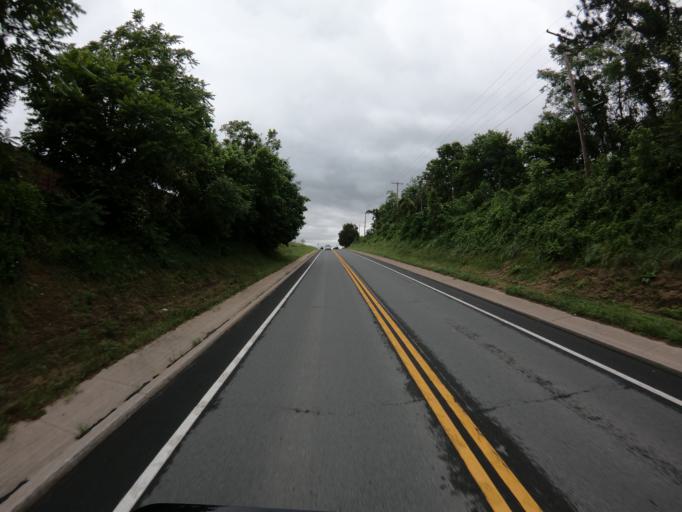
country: US
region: West Virginia
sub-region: Jefferson County
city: Shepherdstown
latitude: 39.4454
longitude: -77.7755
